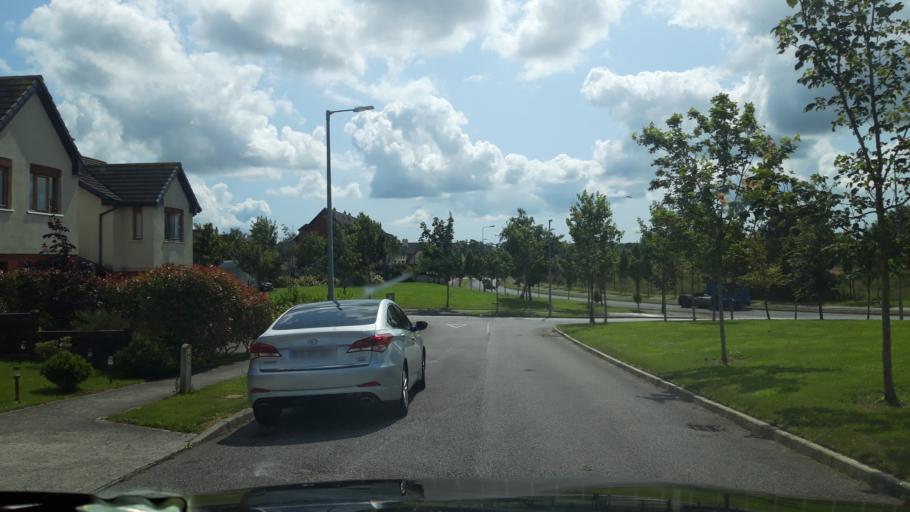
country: IE
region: Munster
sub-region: Waterford
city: Waterford
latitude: 52.2704
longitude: -7.0879
